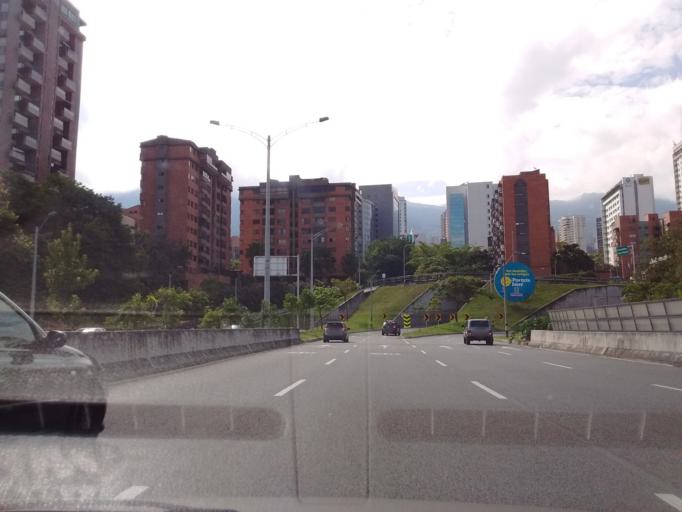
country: CO
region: Antioquia
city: Itagui
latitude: 6.2025
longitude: -75.5762
